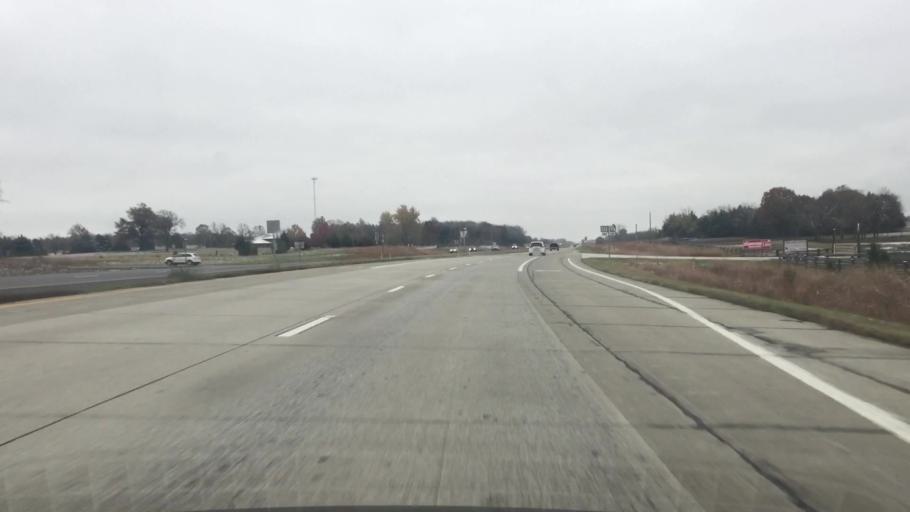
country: US
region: Missouri
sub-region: Saint Clair County
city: Osceola
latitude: 38.0107
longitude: -93.6582
